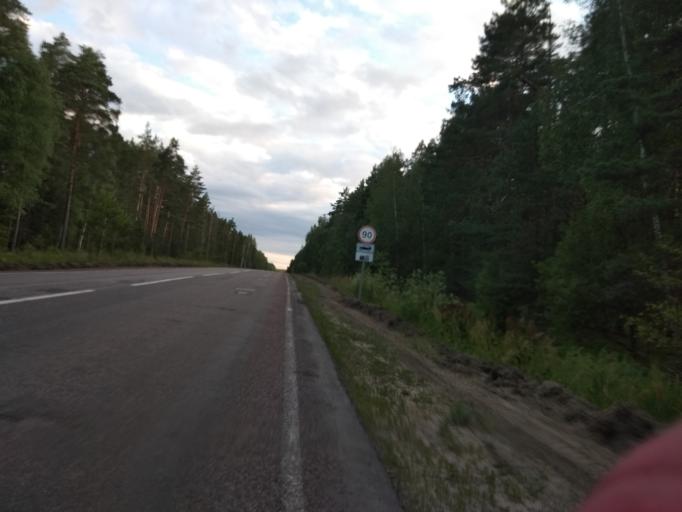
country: RU
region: Moskovskaya
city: Misheronskiy
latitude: 55.6397
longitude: 39.7523
